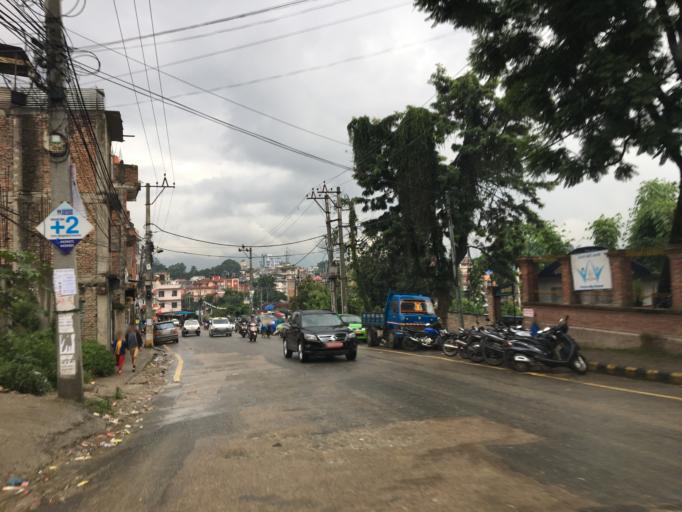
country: NP
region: Central Region
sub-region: Bagmati Zone
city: Kathmandu
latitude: 27.7121
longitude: 85.3391
